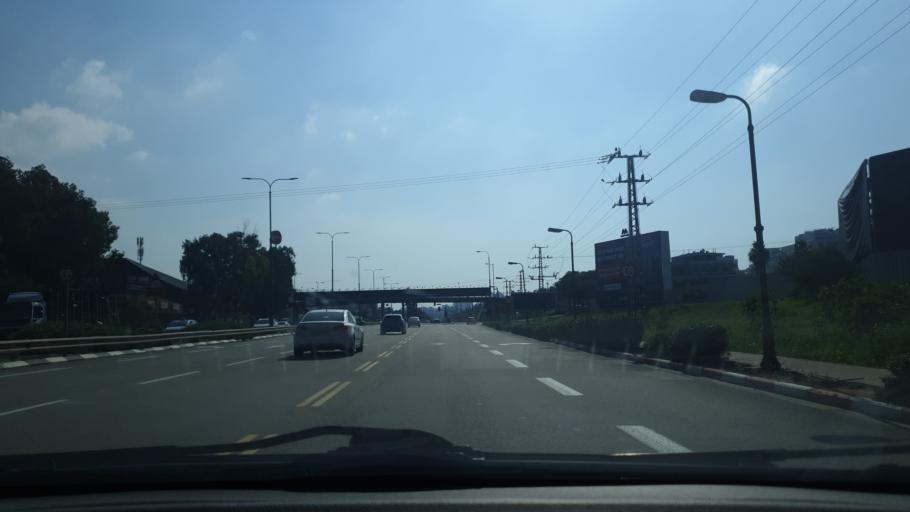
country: IL
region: Central District
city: Bet Dagan
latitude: 31.9857
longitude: 34.8108
